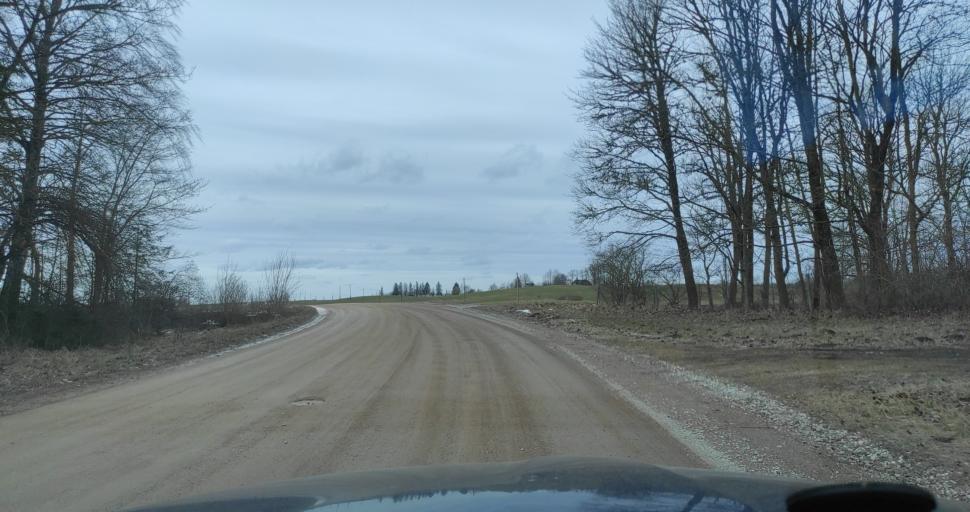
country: LV
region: Tukuma Rajons
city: Tukums
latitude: 57.0172
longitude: 23.0342
